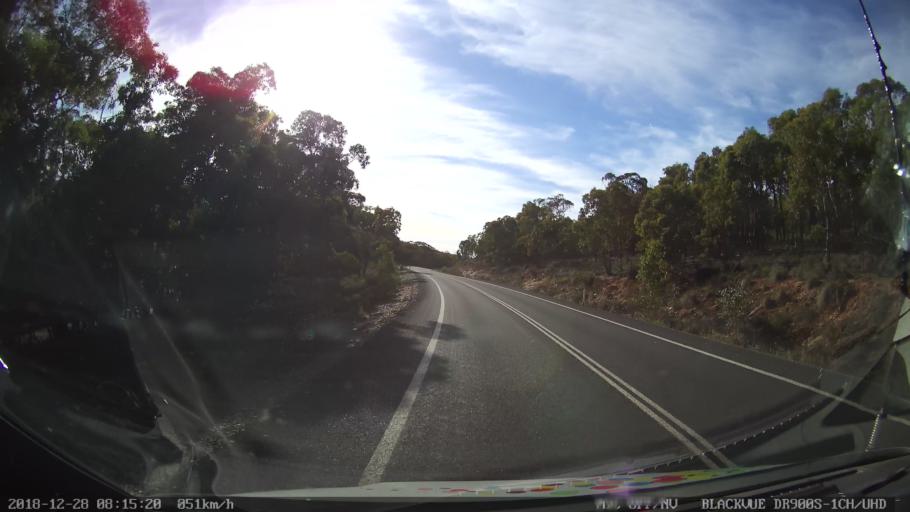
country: AU
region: New South Wales
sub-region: Blayney
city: Blayney
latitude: -33.8228
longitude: 149.3274
